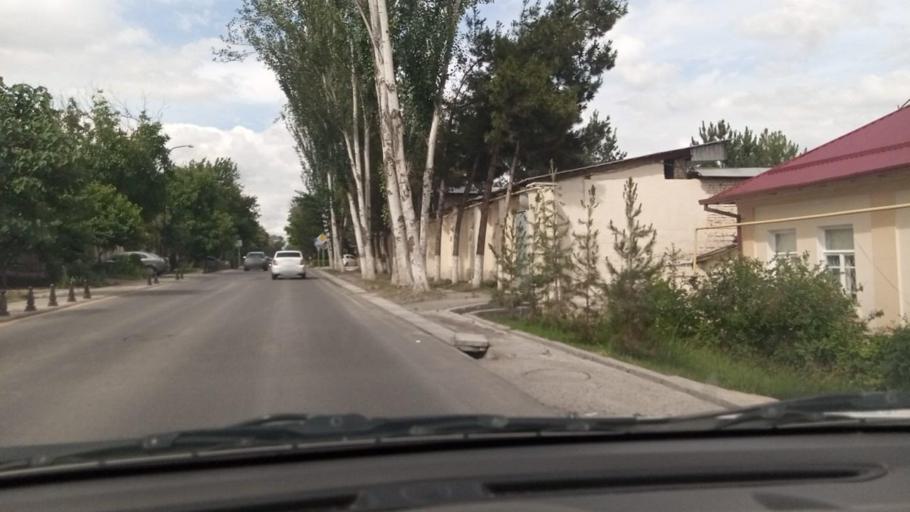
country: UZ
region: Toshkent
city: Salor
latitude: 41.3297
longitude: 69.3554
